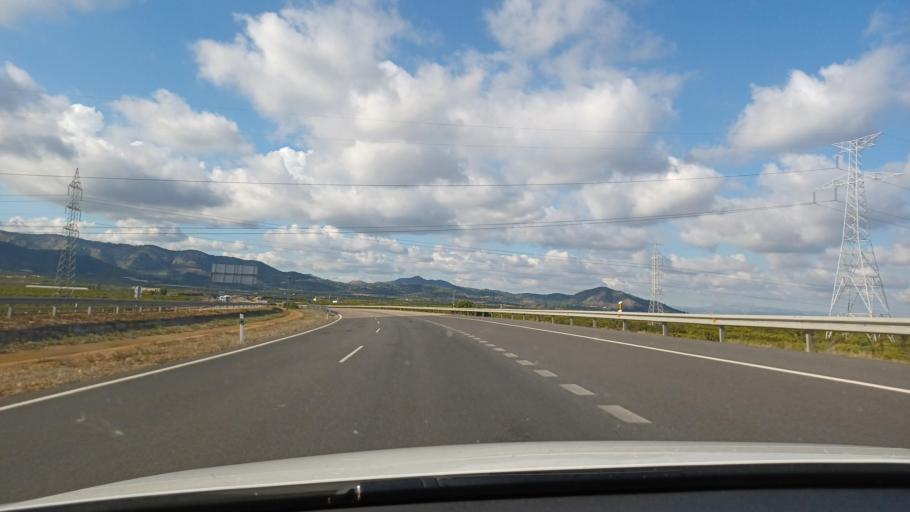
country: ES
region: Valencia
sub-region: Provincia de Castello
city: Nules
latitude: 39.8645
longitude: -0.1708
